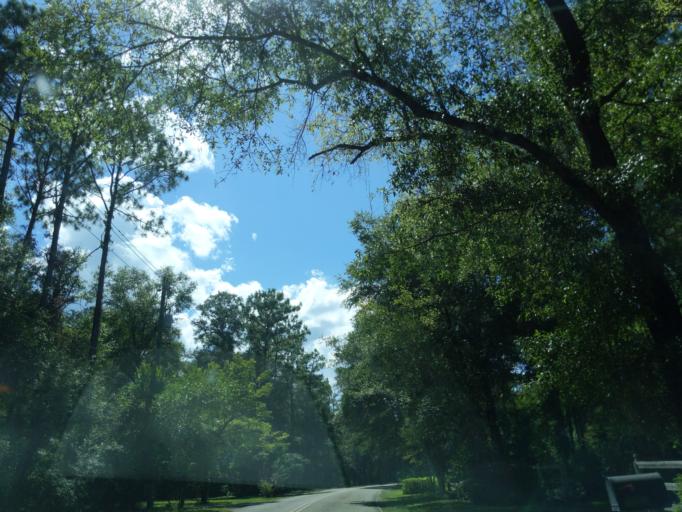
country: US
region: Florida
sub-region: Leon County
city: Tallahassee
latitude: 30.3995
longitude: -84.3397
